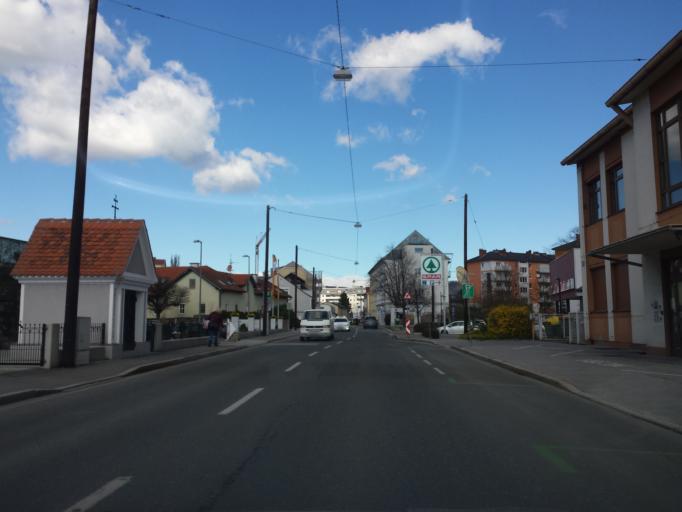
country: AT
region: Styria
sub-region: Graz Stadt
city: Goesting
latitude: 47.0874
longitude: 15.4190
